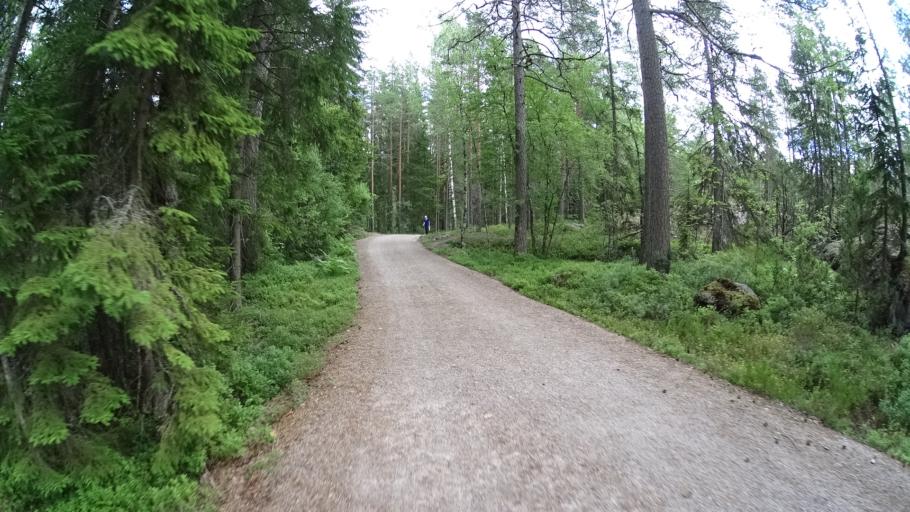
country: FI
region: Uusimaa
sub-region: Helsinki
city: Espoo
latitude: 60.2723
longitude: 24.6248
